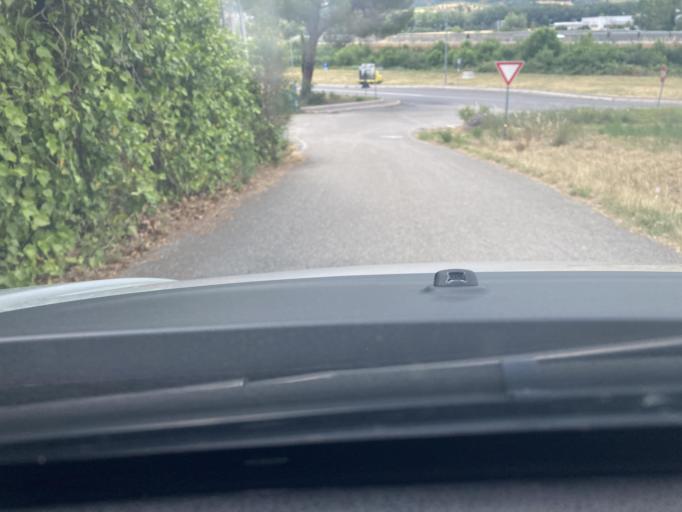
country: IT
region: Umbria
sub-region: Provincia di Perugia
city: Corciano
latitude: 43.1313
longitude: 12.2639
